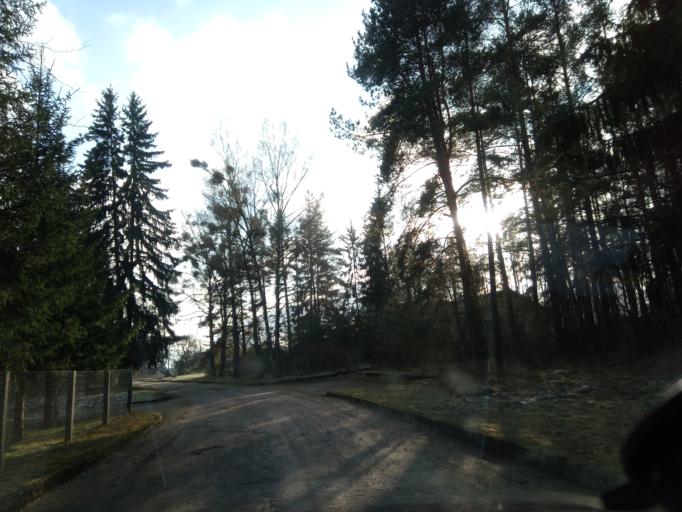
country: LT
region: Alytaus apskritis
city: Druskininkai
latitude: 53.9531
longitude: 24.2934
